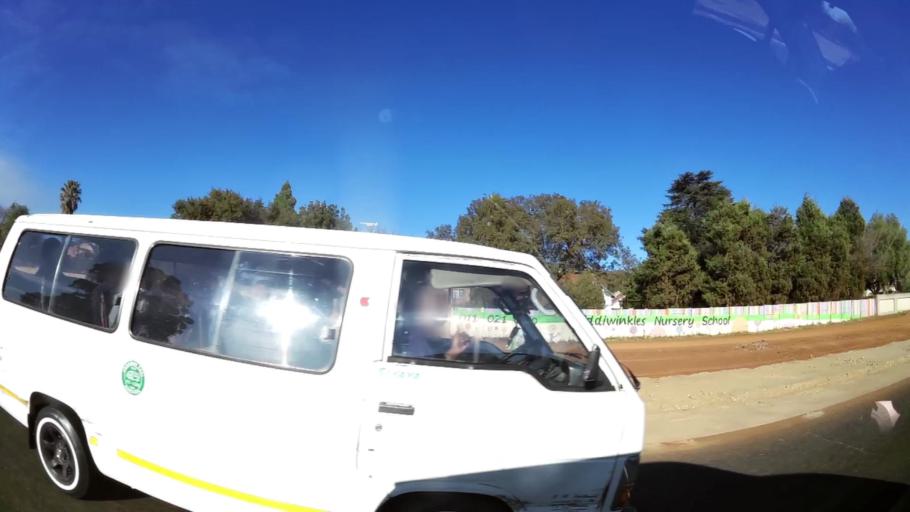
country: ZA
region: Gauteng
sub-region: City of Johannesburg Metropolitan Municipality
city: Roodepoort
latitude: -26.1132
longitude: 27.8887
